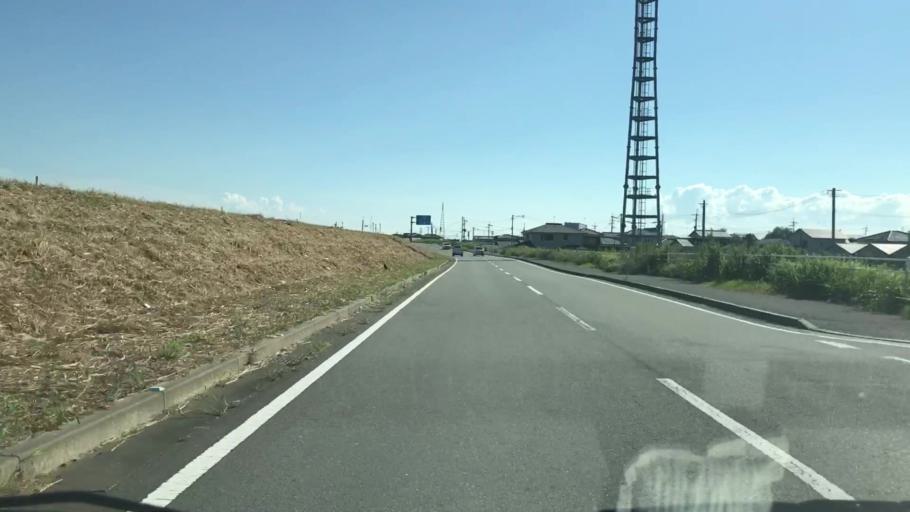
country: JP
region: Saga Prefecture
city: Okawa
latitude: 33.2392
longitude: 130.3814
